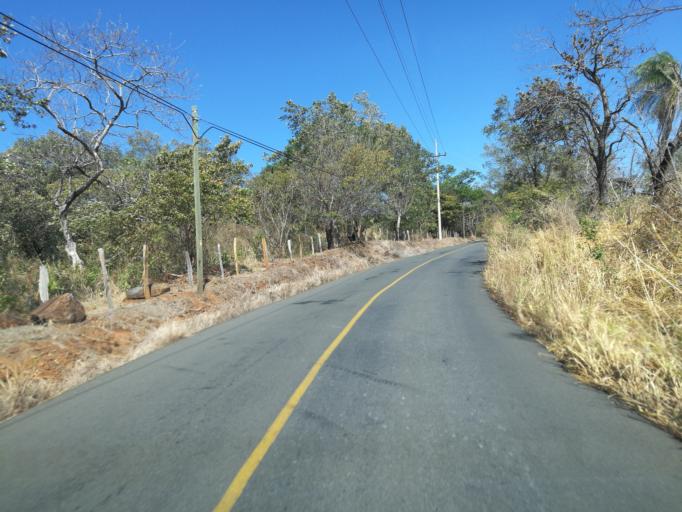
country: CR
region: Guanacaste
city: Liberia
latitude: 10.6681
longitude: -85.4666
